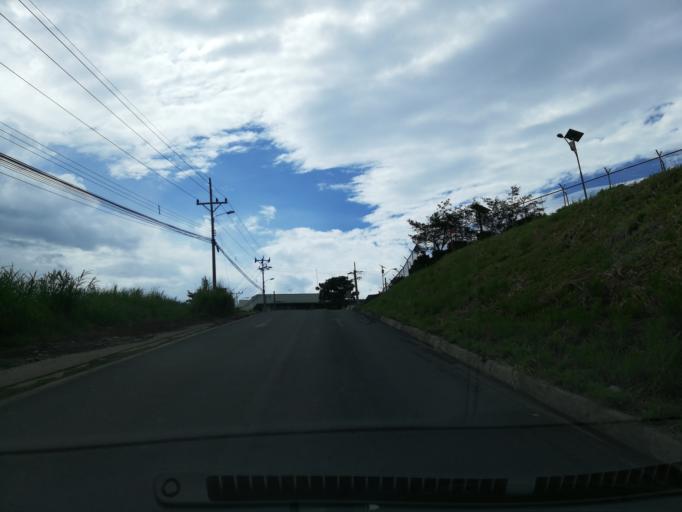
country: CR
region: Alajuela
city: Alajuela
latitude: 9.9980
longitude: -84.2139
